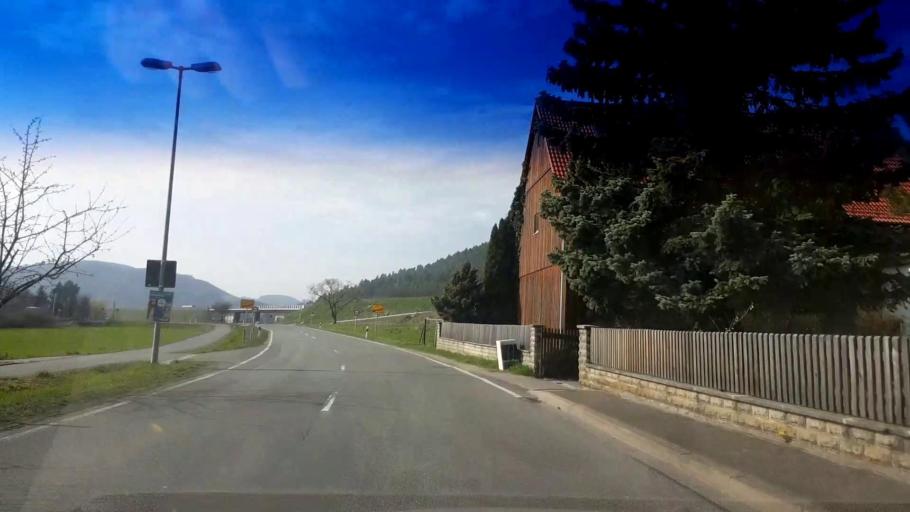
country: DE
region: Bavaria
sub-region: Upper Franconia
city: Harsdorf
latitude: 50.0310
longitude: 11.5633
